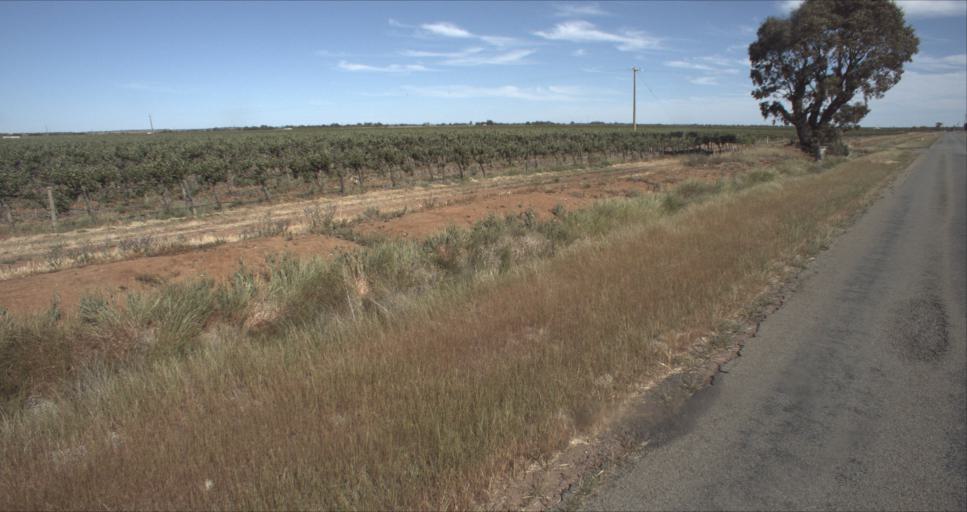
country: AU
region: New South Wales
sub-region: Leeton
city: Leeton
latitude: -34.5777
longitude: 146.3804
